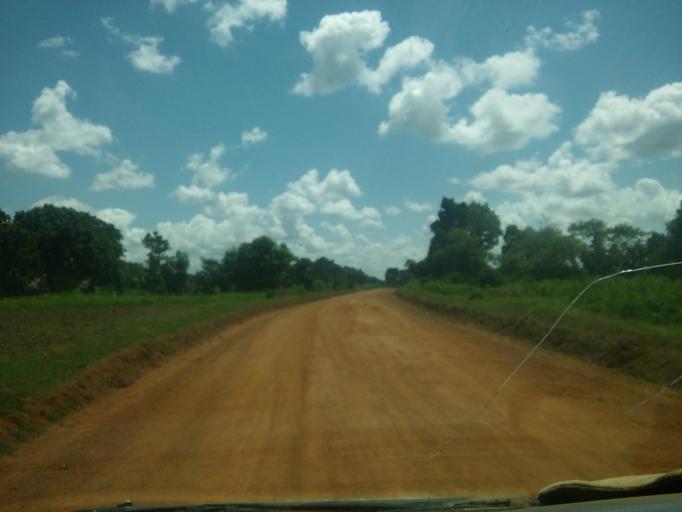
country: UG
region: Eastern Region
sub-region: Budaka District
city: Budaka
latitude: 1.1148
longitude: 33.9463
